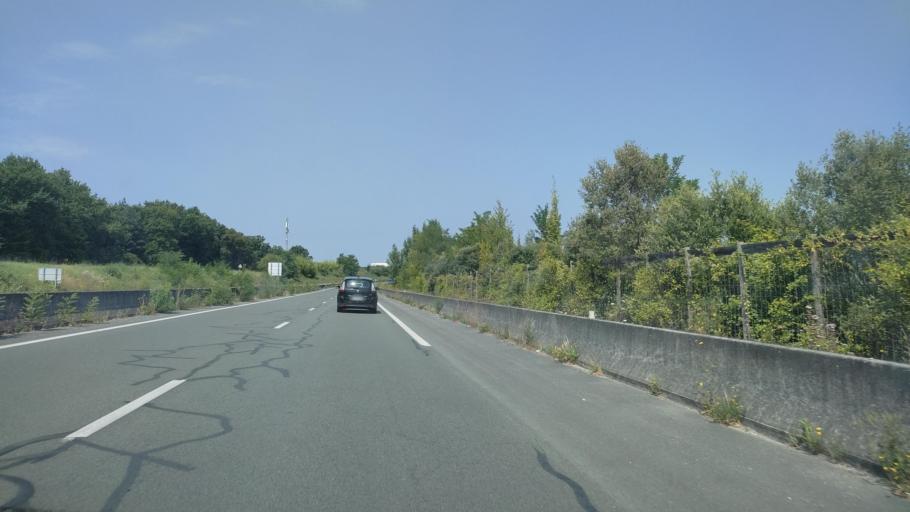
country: FR
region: Poitou-Charentes
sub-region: Departement de la Charente
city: Saint-Yrieix-sur-Charente
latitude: 45.6822
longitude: 0.1204
